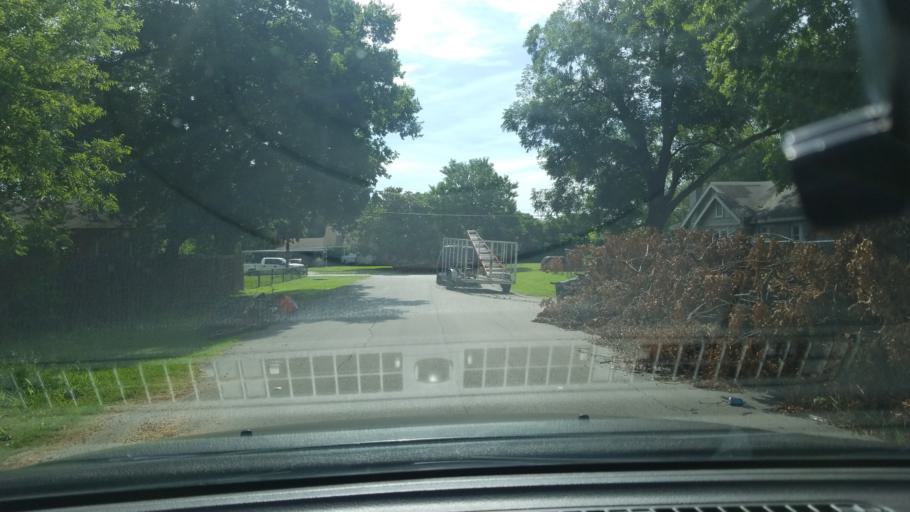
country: US
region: Texas
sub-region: Dallas County
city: Balch Springs
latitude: 32.7648
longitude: -96.6708
